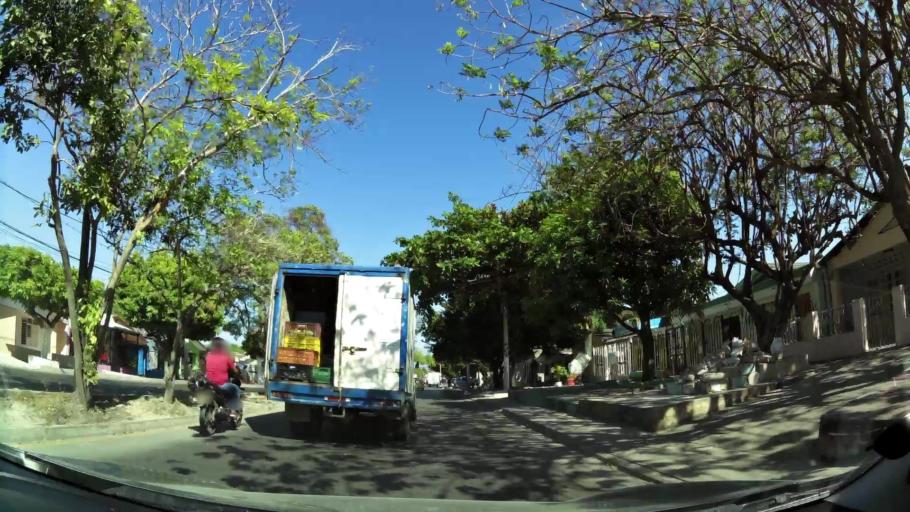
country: CO
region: Atlantico
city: Barranquilla
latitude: 10.9461
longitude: -74.8015
